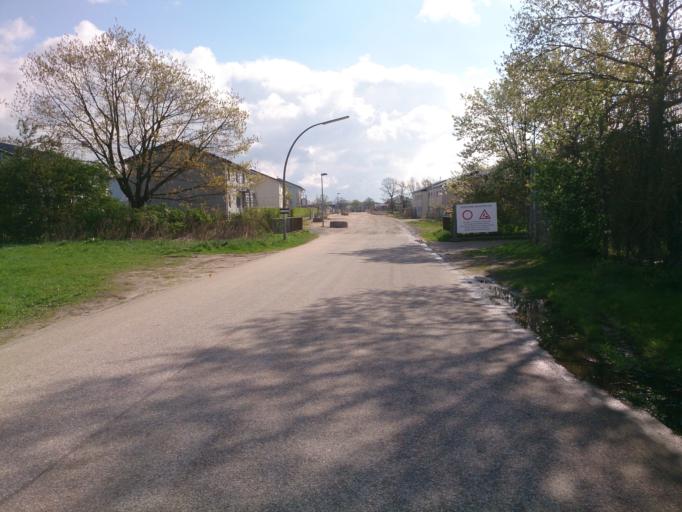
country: DE
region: Lower Saxony
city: Neu Wulmstorf
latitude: 53.4762
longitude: 9.8403
